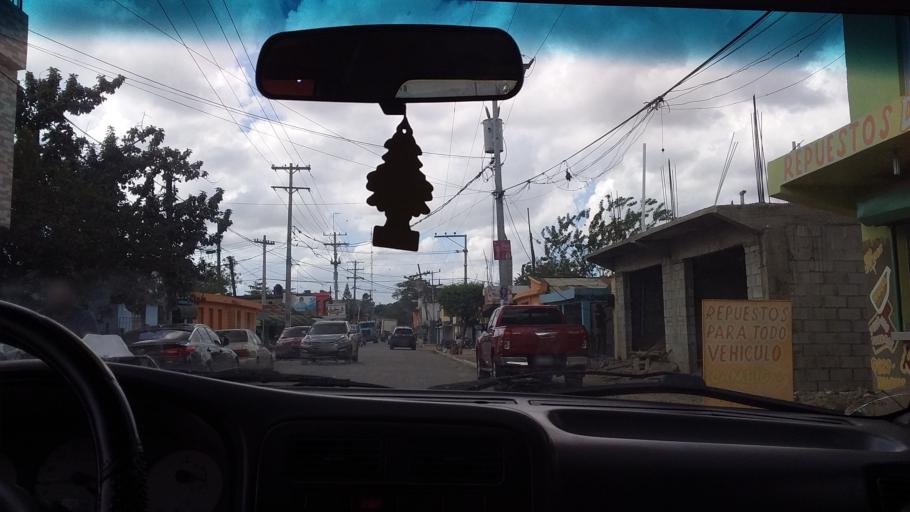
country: DO
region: Santo Domingo
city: Guerra
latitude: 18.5587
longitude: -69.7013
